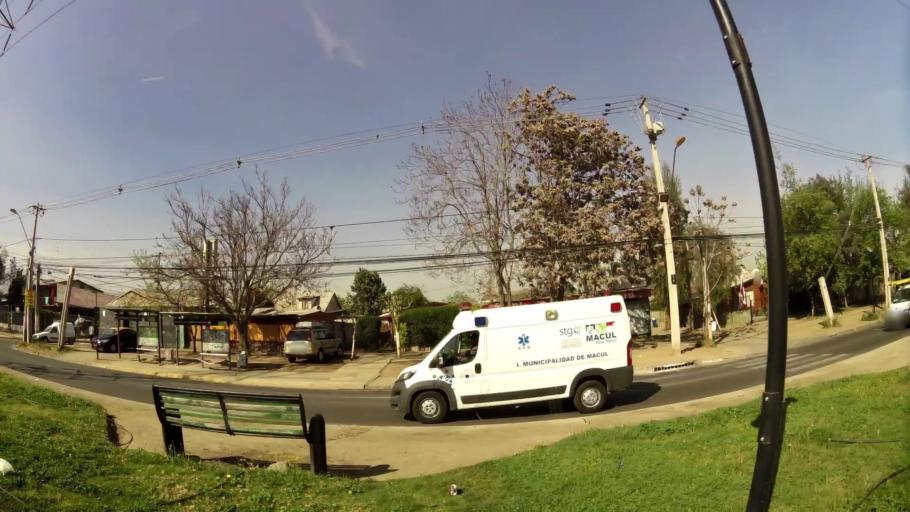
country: CL
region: Santiago Metropolitan
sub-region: Provincia de Santiago
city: Villa Presidente Frei, Nunoa, Santiago, Chile
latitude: -33.5006
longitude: -70.5844
